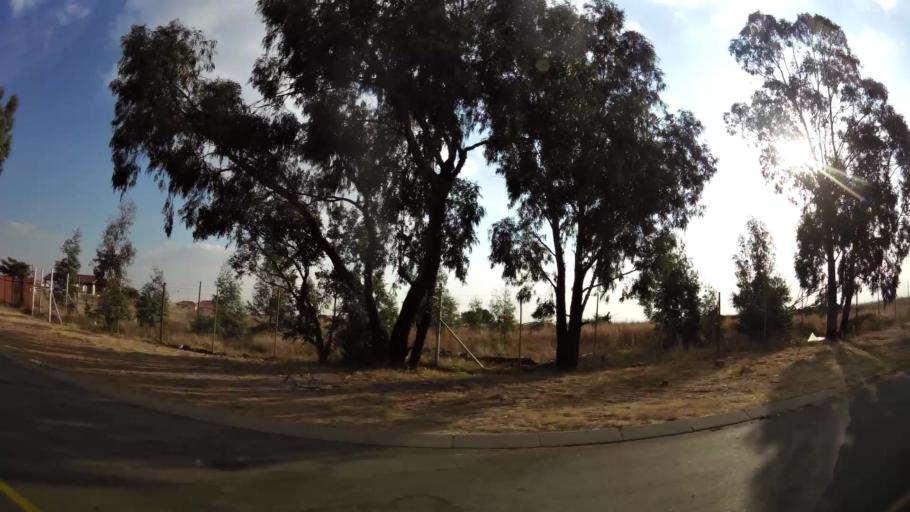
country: ZA
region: Gauteng
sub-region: West Rand District Municipality
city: Krugersdorp
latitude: -26.0982
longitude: 27.7330
